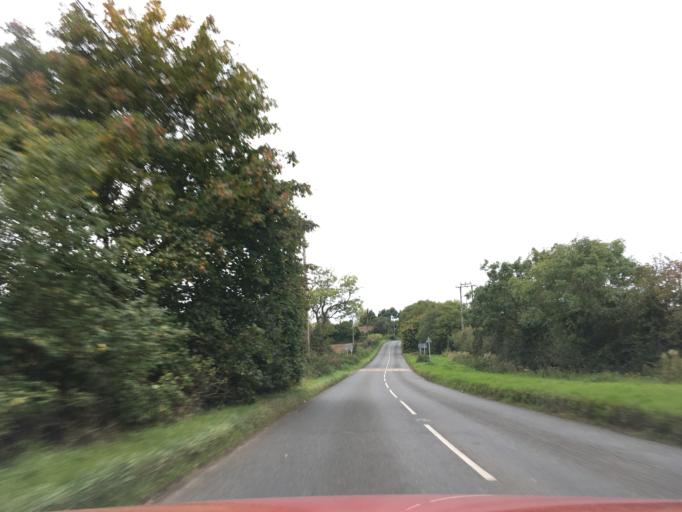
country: GB
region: England
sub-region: South Gloucestershire
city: Almondsbury
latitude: 51.5946
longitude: -2.5837
